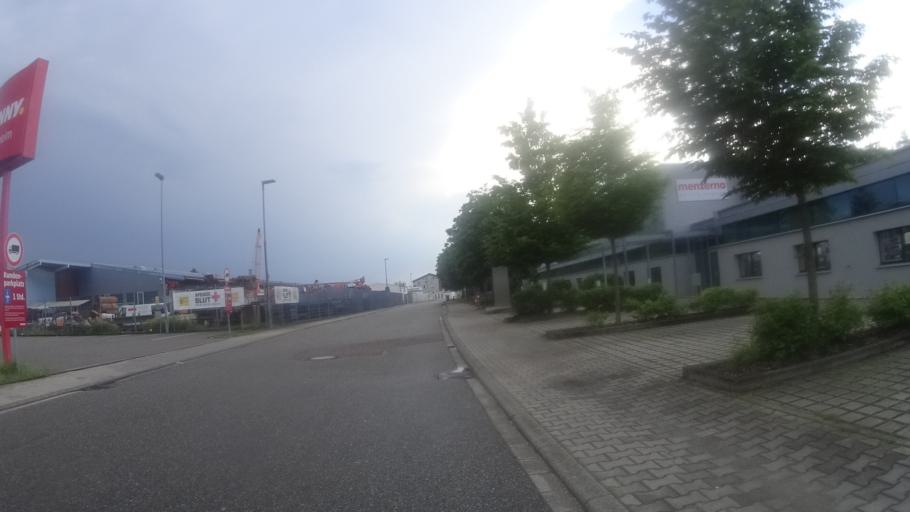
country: DE
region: Baden-Wuerttemberg
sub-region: Karlsruhe Region
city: Otigheim
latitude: 48.8868
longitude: 8.2432
